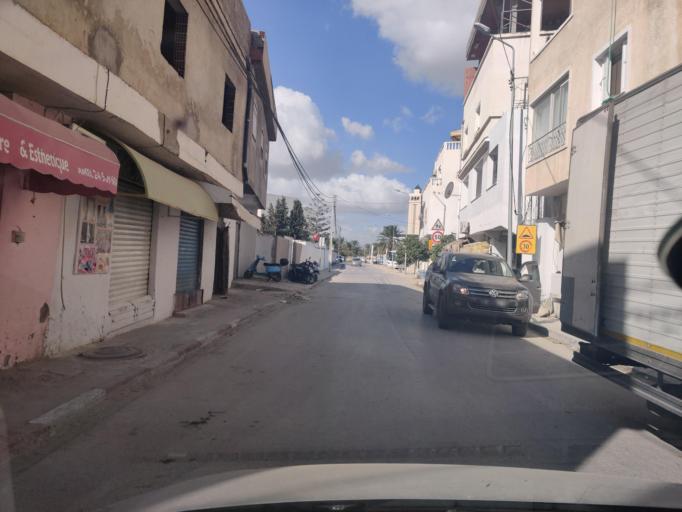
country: TN
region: Tunis
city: Al Marsa
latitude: 36.8779
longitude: 10.2681
